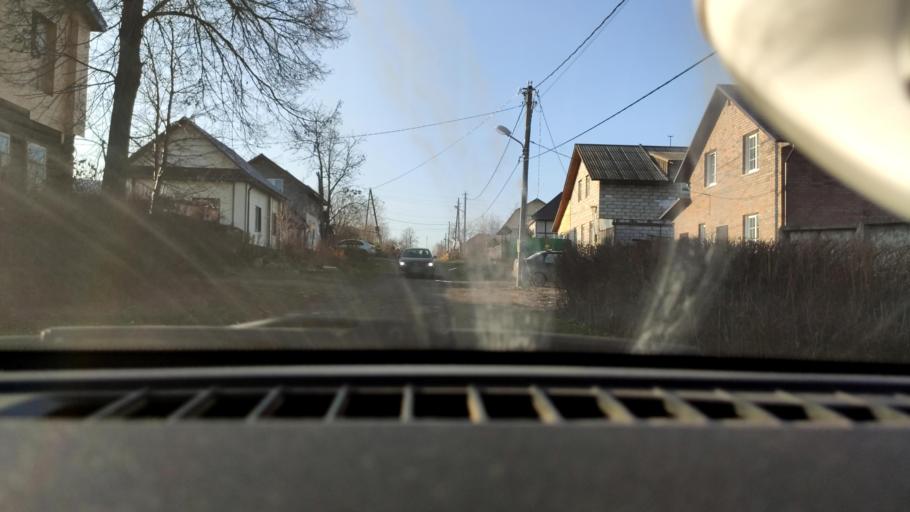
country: RU
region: Perm
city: Perm
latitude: 58.0171
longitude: 56.3184
